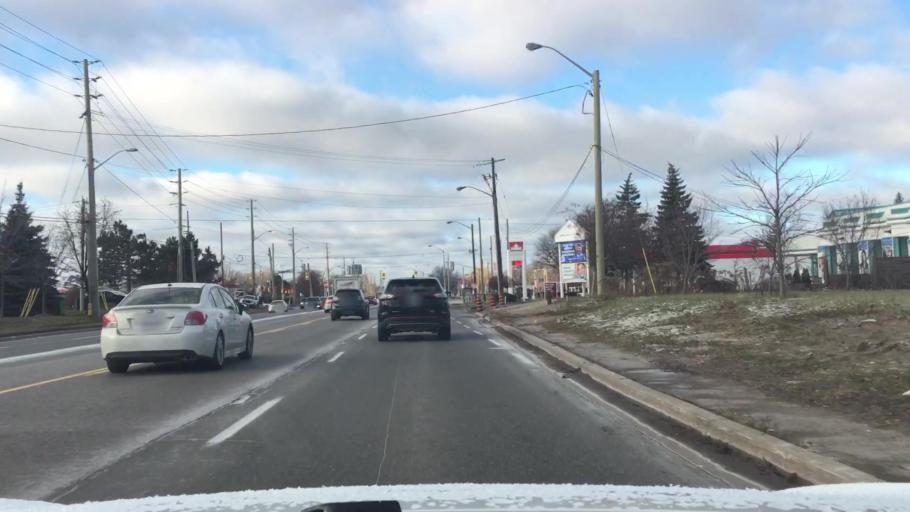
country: CA
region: Ontario
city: Markham
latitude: 43.8632
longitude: -79.3018
